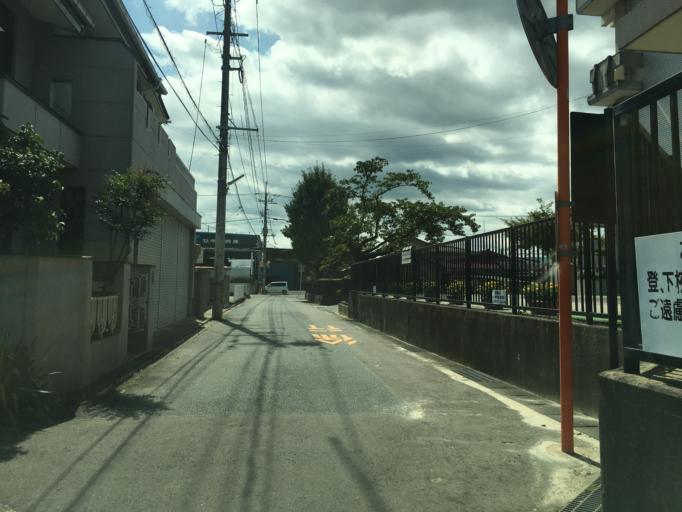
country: JP
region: Fukushima
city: Fukushima-shi
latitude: 37.7446
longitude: 140.4331
